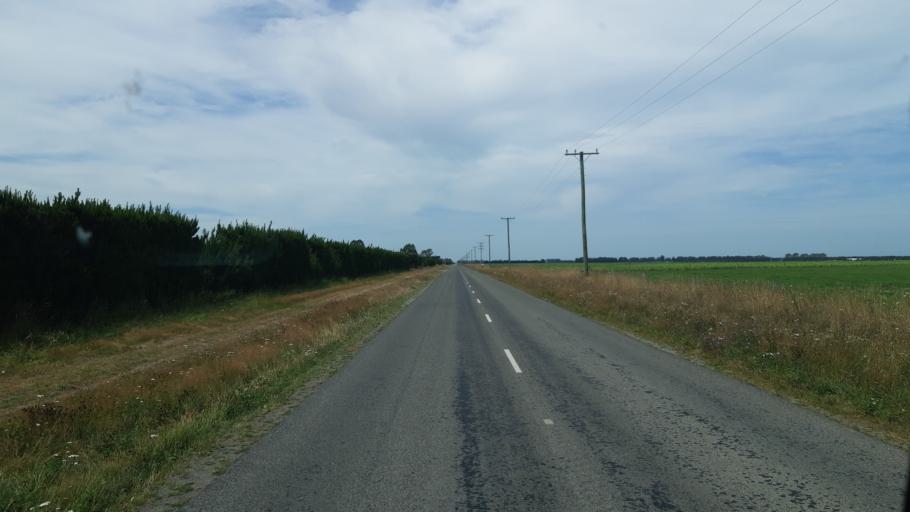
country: NZ
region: Canterbury
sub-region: Ashburton District
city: Tinwald
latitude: -43.9247
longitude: 171.5611
